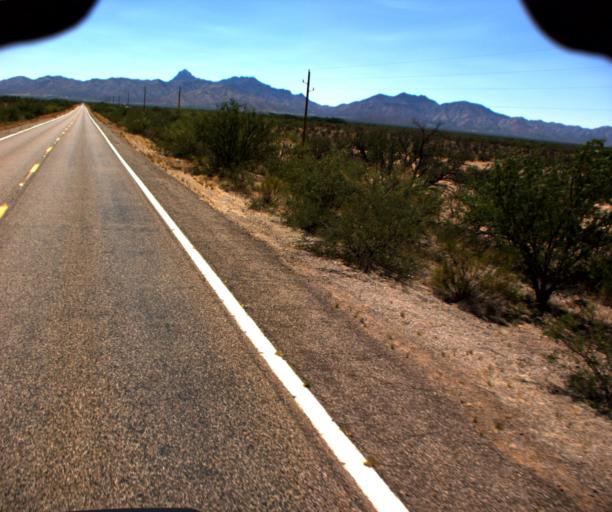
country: US
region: Arizona
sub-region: Pima County
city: Three Points
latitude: 31.8385
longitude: -111.4053
